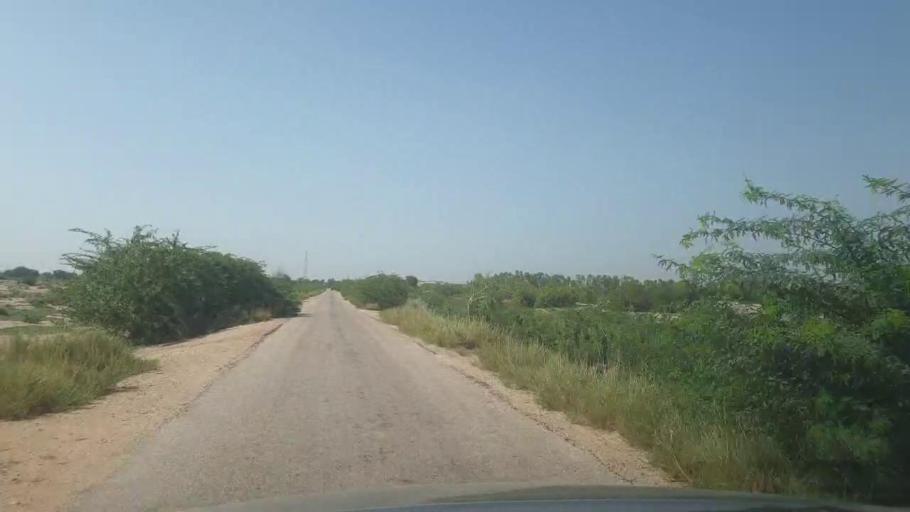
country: PK
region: Sindh
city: Rohri
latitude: 27.4168
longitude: 69.0801
